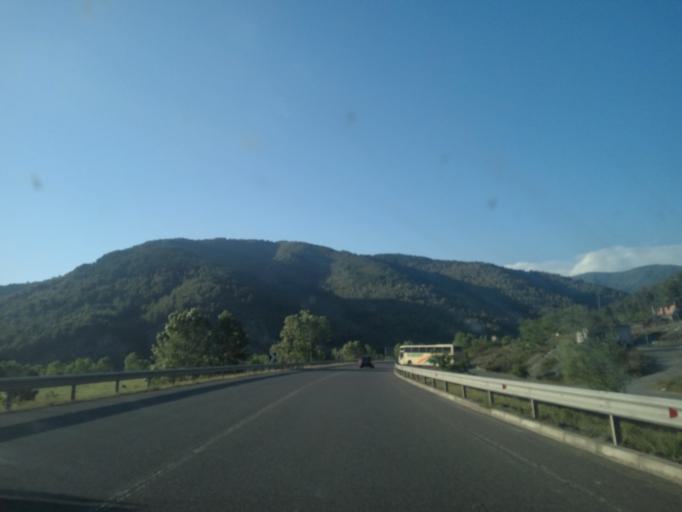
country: AL
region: Lezhe
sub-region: Rrethi i Mirdites
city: Rubik
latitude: 41.7808
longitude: 19.7837
